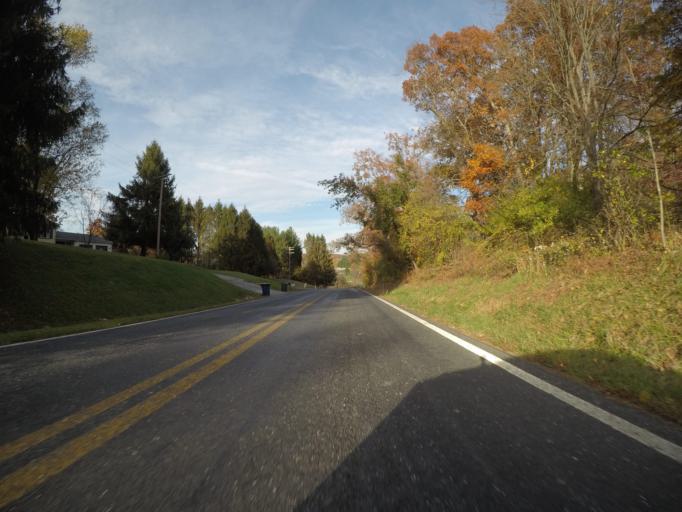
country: US
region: Maryland
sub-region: Carroll County
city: Hampstead
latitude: 39.5731
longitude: -76.8994
